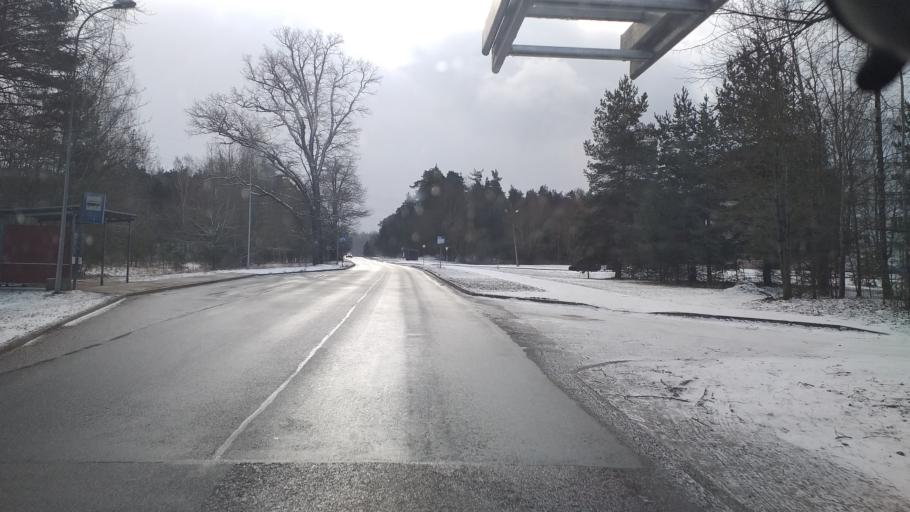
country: LV
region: Riga
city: Bolderaja
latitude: 56.9844
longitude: 24.0327
